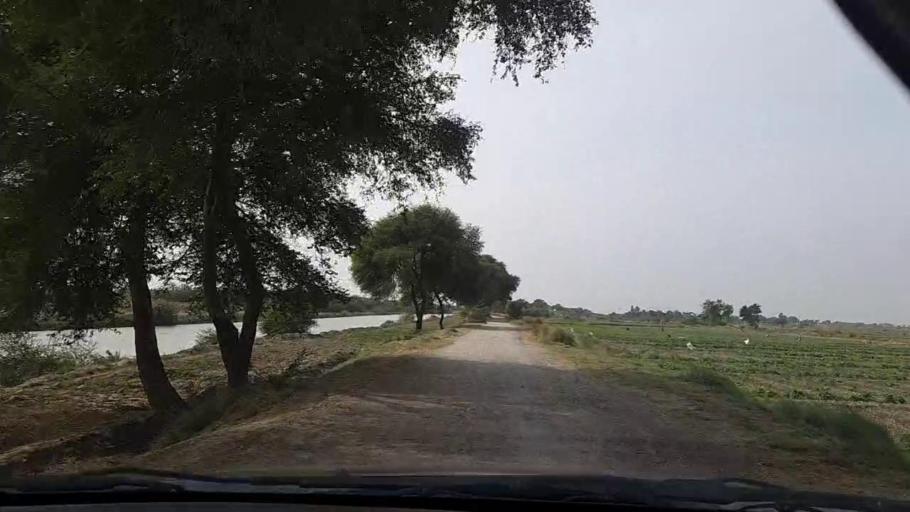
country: PK
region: Sindh
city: Thatta
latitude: 24.5689
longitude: 67.8672
